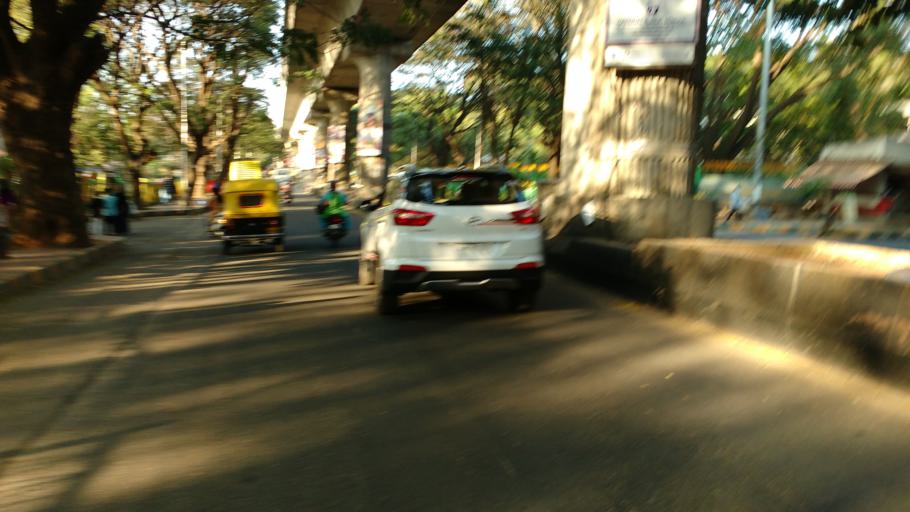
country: IN
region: Karnataka
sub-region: Bangalore Urban
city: Bangalore
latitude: 12.9328
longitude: 77.5801
